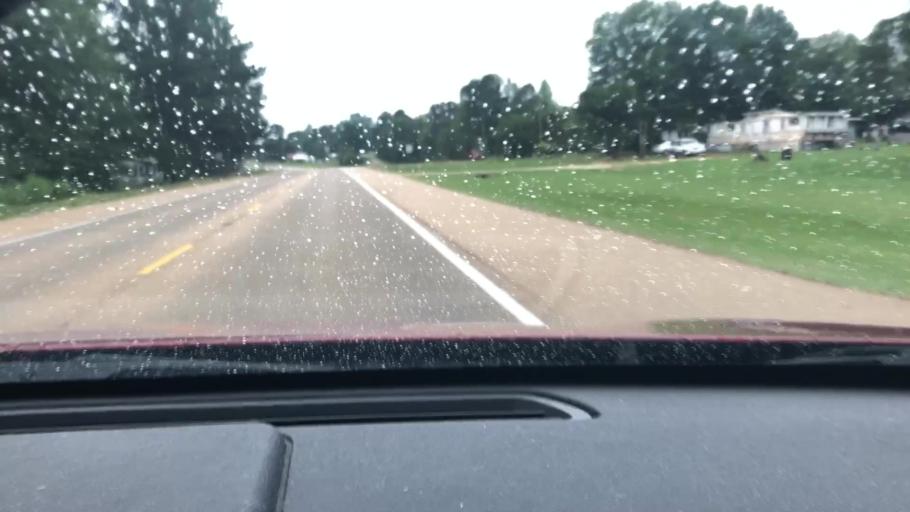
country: US
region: Arkansas
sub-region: Lafayette County
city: Stamps
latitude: 33.3590
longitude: -93.4265
